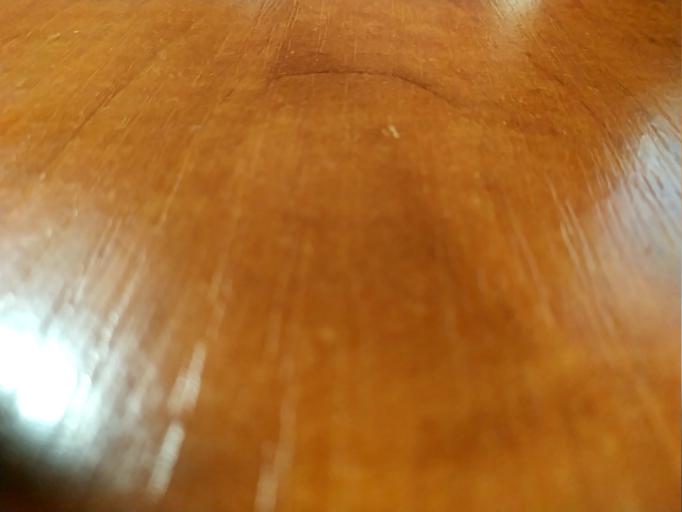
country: RU
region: Tverskaya
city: Vyshniy Volochek
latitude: 57.3971
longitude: 34.5243
